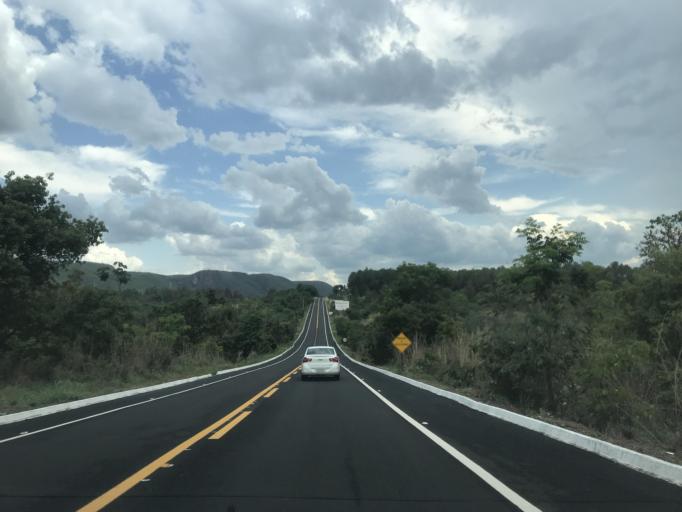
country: BR
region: Goias
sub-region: Caldas Novas
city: Caldas Novas
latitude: -17.7536
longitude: -48.7568
